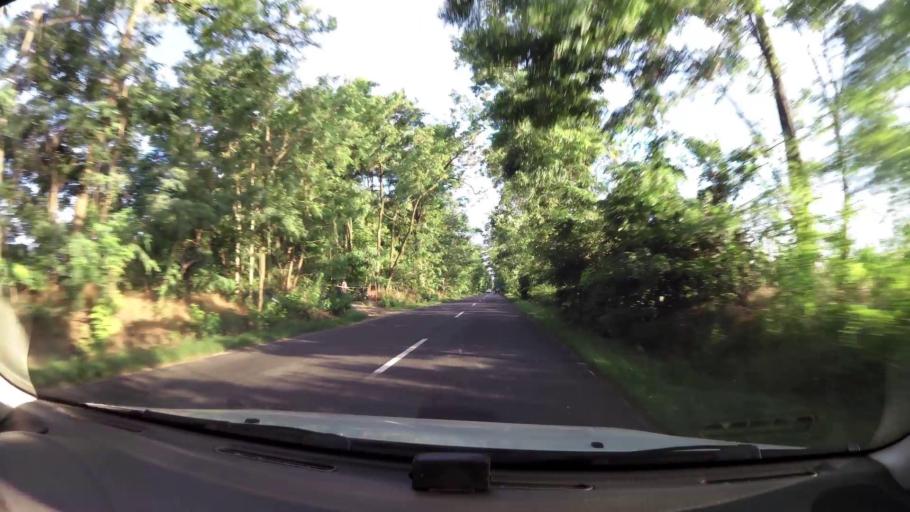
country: HU
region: Pest
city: Tapiosag
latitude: 47.4194
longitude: 19.6093
